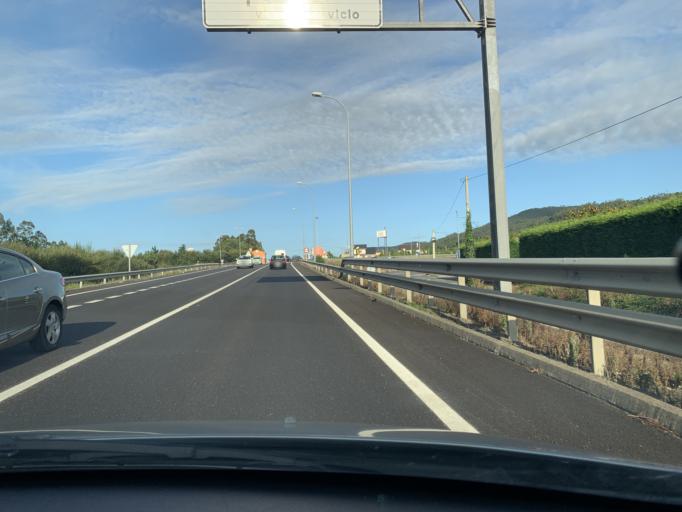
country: ES
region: Galicia
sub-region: Provincia de Lugo
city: Barreiros
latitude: 43.5403
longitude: -7.2541
